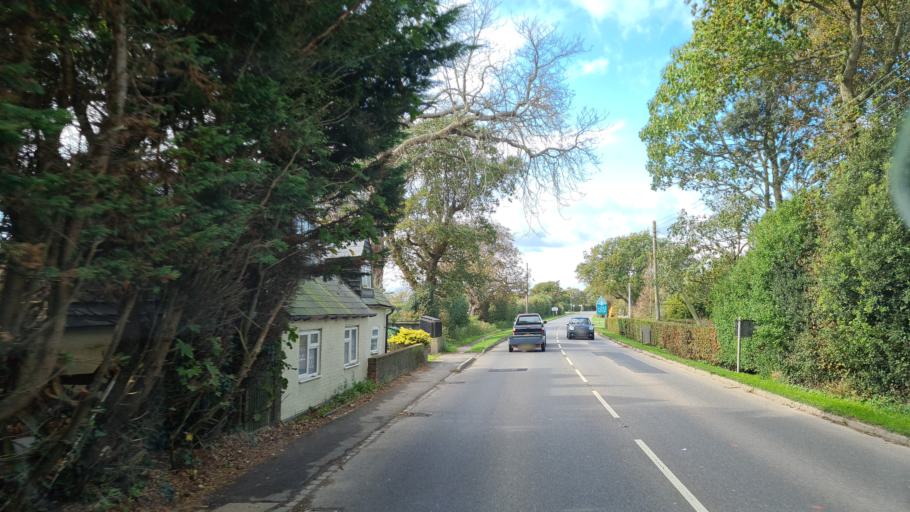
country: GB
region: England
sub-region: East Sussex
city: Bodle Street
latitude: 50.8870
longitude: 0.3338
